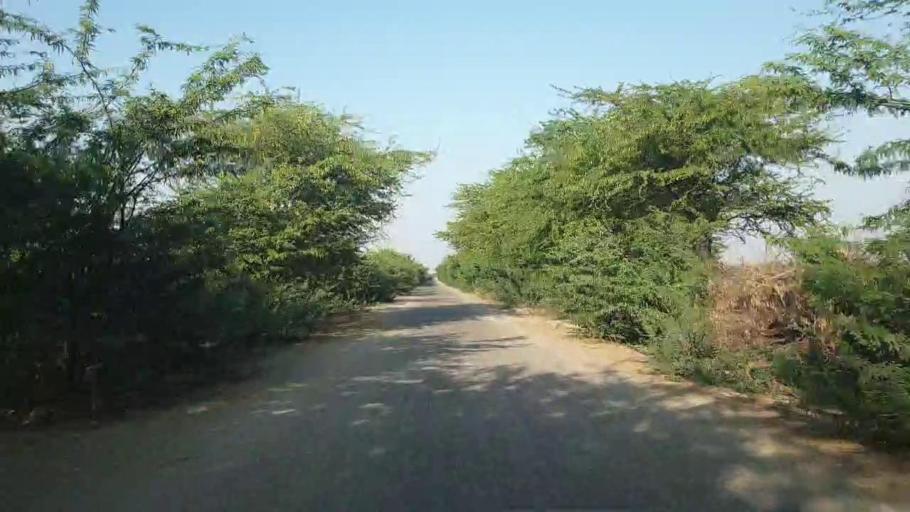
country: PK
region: Sindh
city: Chor
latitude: 25.5529
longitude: 69.7901
